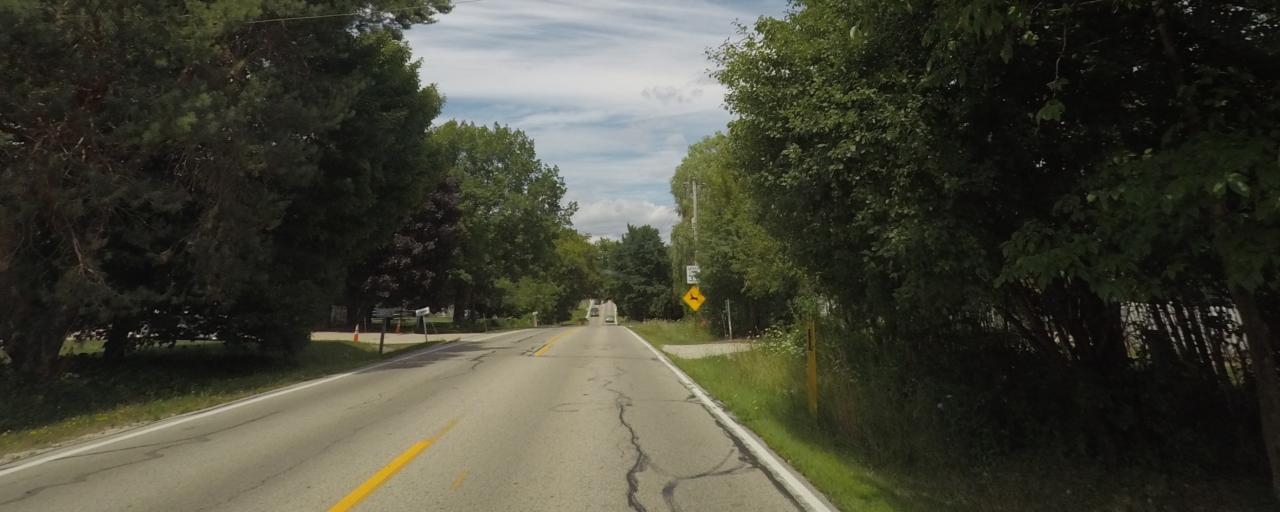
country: US
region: Wisconsin
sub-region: Milwaukee County
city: Hales Corners
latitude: 42.9699
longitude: -88.0690
